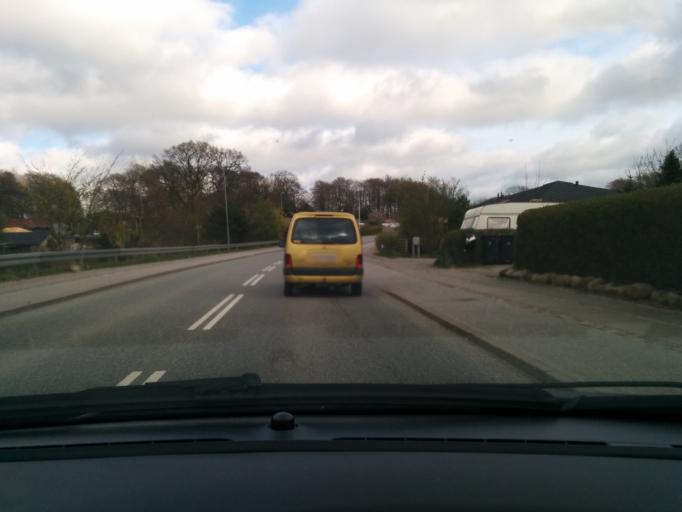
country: DK
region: Central Jutland
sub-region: Favrskov Kommune
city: Hadsten
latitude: 56.3265
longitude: 10.0576
